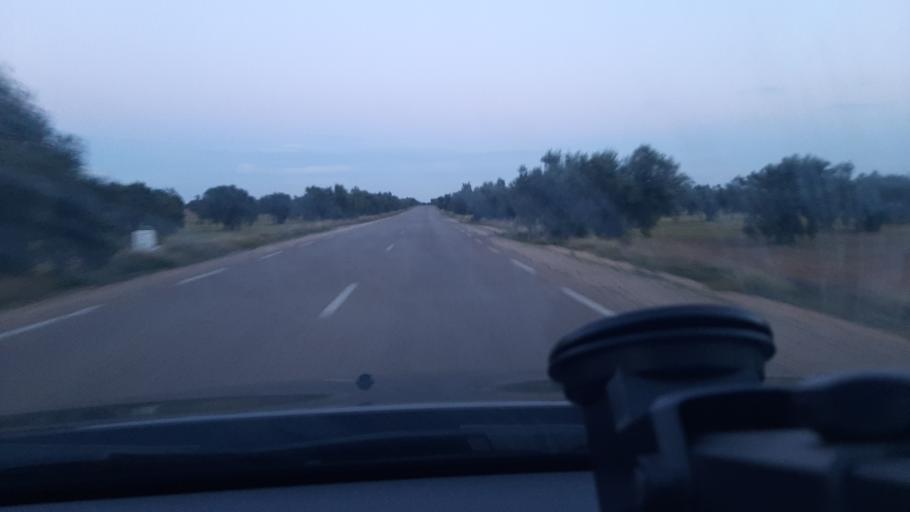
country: TN
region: Al Mahdiyah
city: Shurban
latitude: 35.0332
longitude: 10.5102
